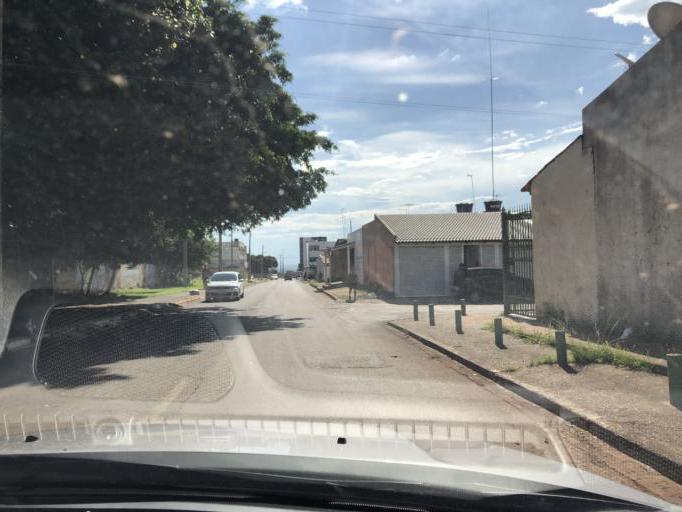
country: BR
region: Federal District
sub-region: Brasilia
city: Brasilia
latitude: -15.7982
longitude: -48.1270
